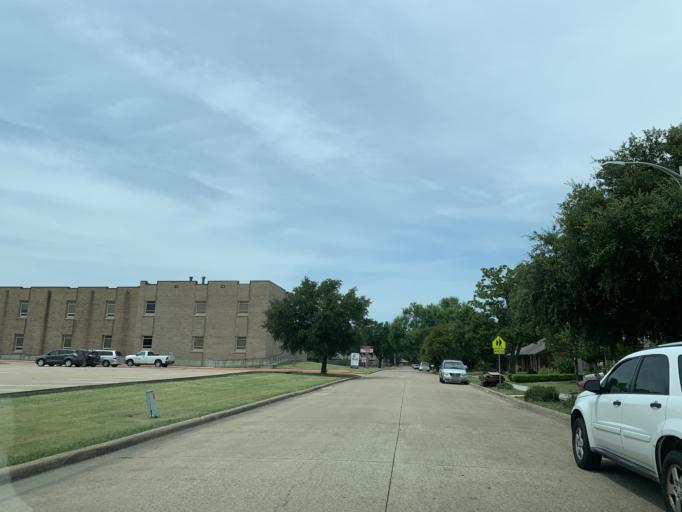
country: US
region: Texas
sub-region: Dallas County
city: Grand Prairie
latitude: 32.6556
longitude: -97.0227
